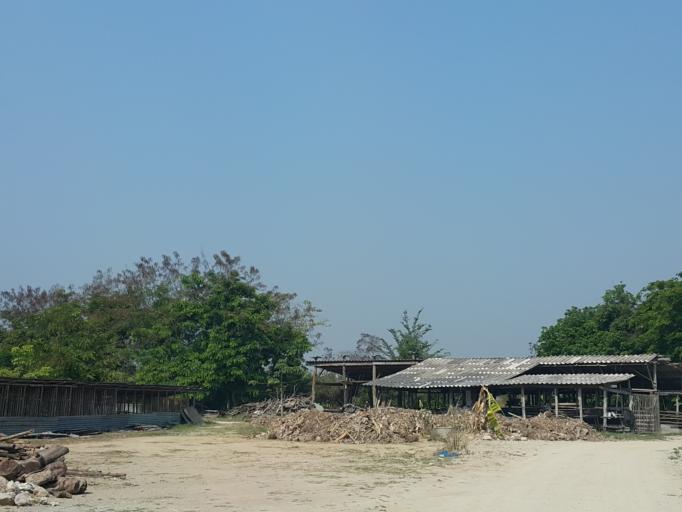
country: TH
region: Chiang Mai
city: San Kamphaeng
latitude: 18.7784
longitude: 99.0773
